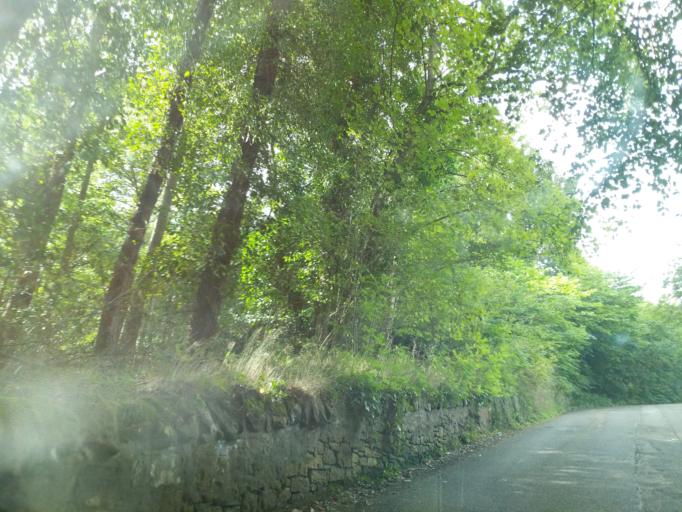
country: GB
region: Scotland
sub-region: Midlothian
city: Loanhead
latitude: 55.8721
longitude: -3.1446
